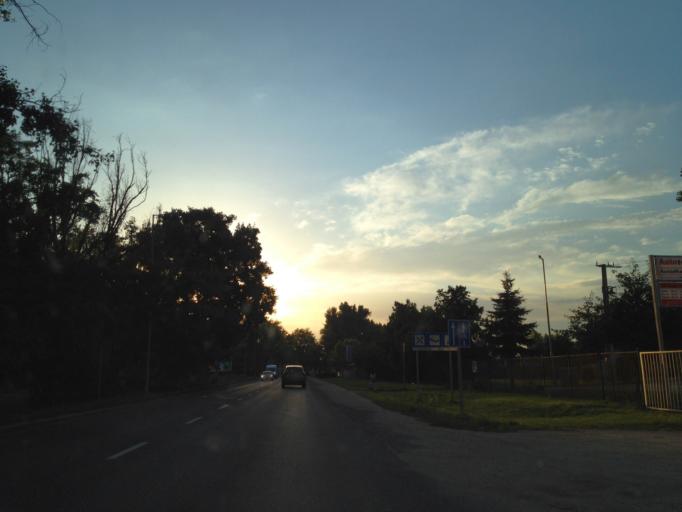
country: HU
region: Gyor-Moson-Sopron
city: Mosonmagyarovar
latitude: 47.8412
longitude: 17.2875
